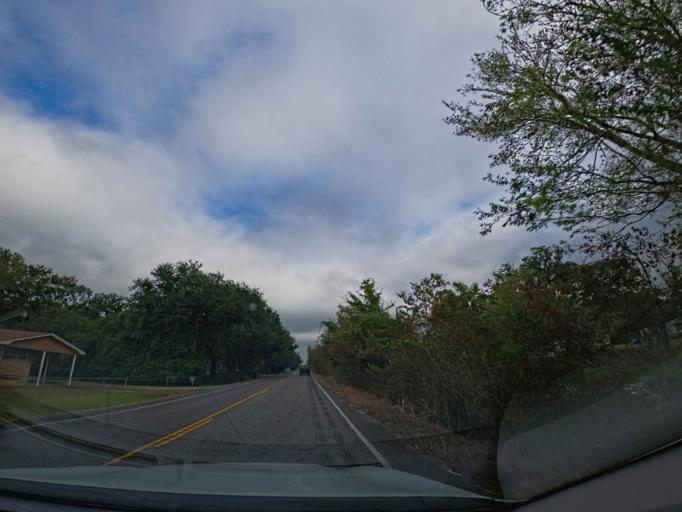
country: US
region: Louisiana
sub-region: Terrebonne Parish
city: Bayou Cane
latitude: 29.5912
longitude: -90.8242
